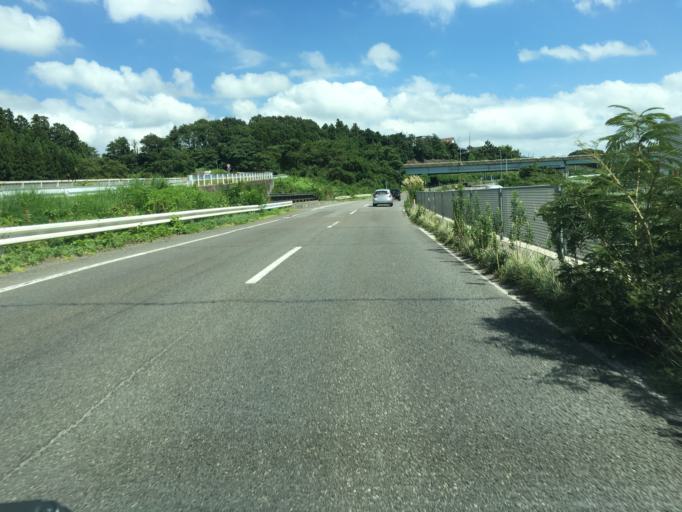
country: JP
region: Fukushima
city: Nihommatsu
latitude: 37.5812
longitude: 140.4245
